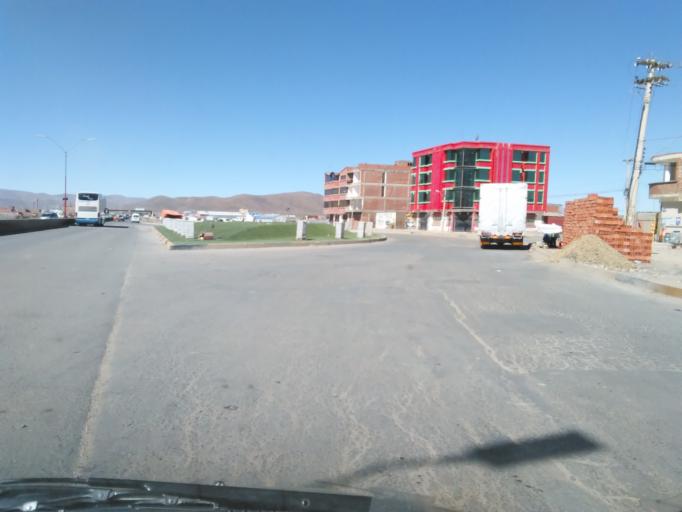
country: BO
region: Oruro
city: Oruro
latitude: -17.9744
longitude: -67.0791
